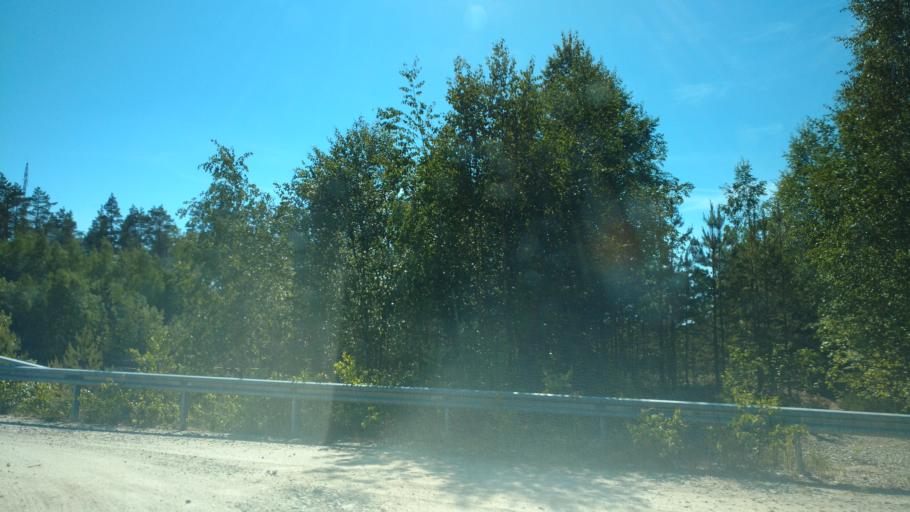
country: FI
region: Varsinais-Suomi
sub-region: Salo
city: Halikko
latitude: 60.4360
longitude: 22.9555
